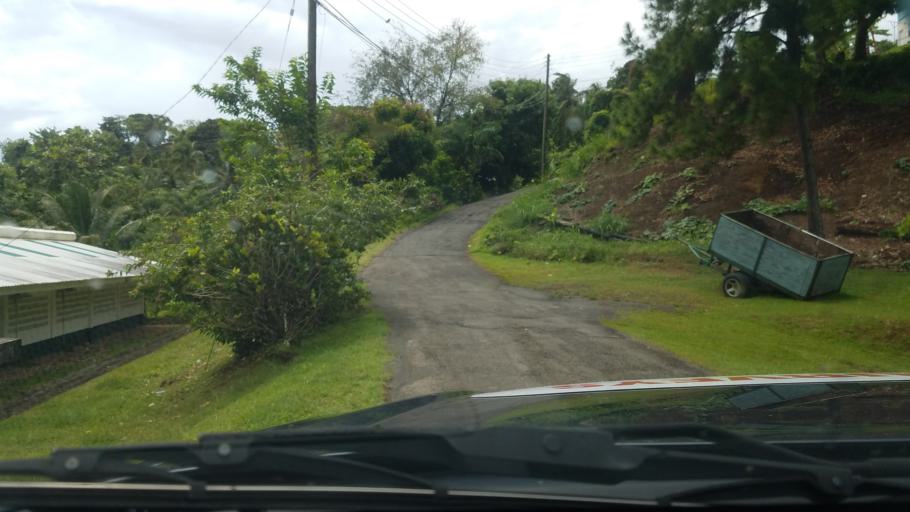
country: LC
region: Castries Quarter
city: Bisee
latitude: 14.0007
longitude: -60.9699
